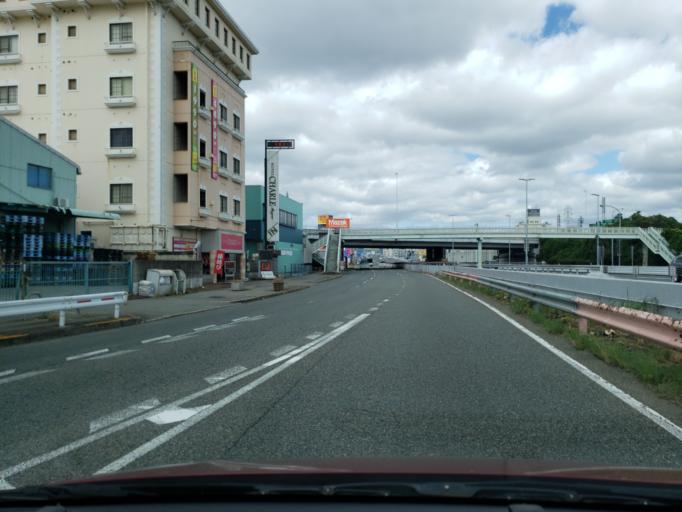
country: JP
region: Osaka
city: Toyonaka
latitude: 34.7513
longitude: 135.4630
